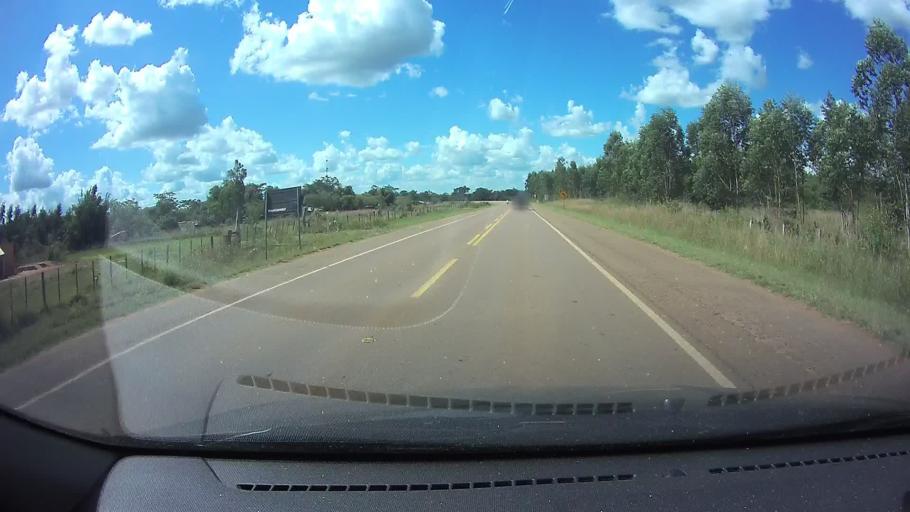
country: PY
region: Guaira
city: Itape
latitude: -25.9054
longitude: -56.6743
